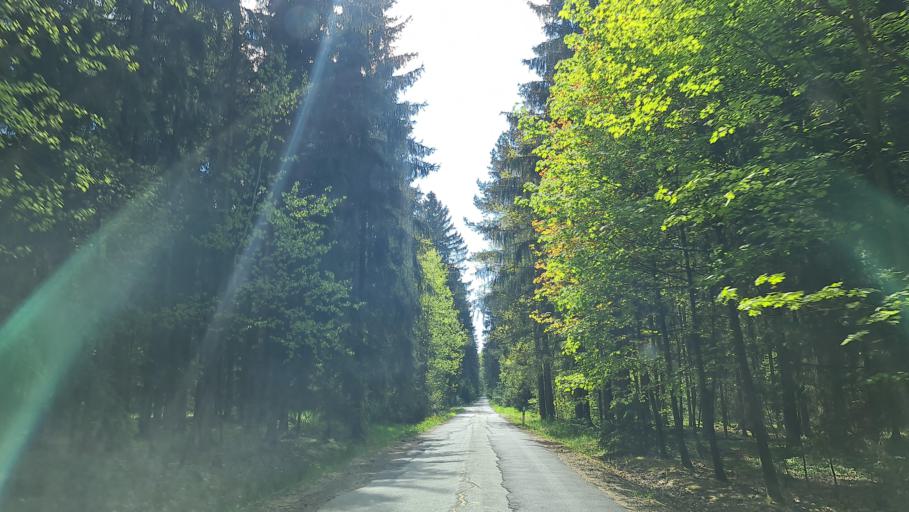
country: DE
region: Thuringia
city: Zeulenroda
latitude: 50.6250
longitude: 12.0168
